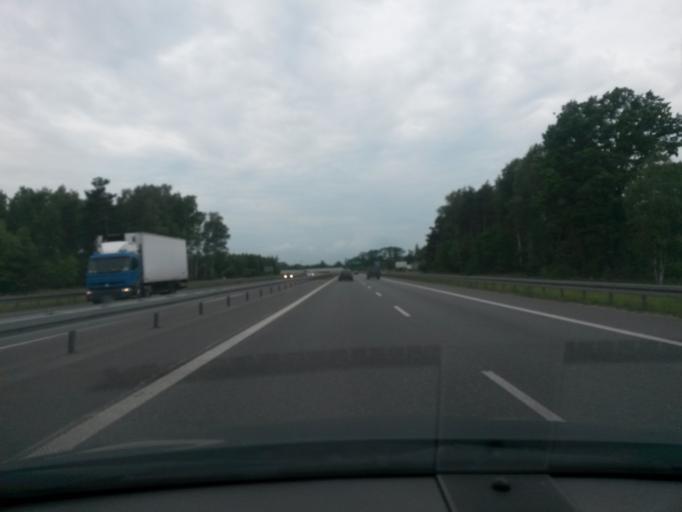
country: PL
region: Masovian Voivodeship
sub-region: Powiat zyrardowski
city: Radziejowice
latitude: 52.0040
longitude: 20.5732
